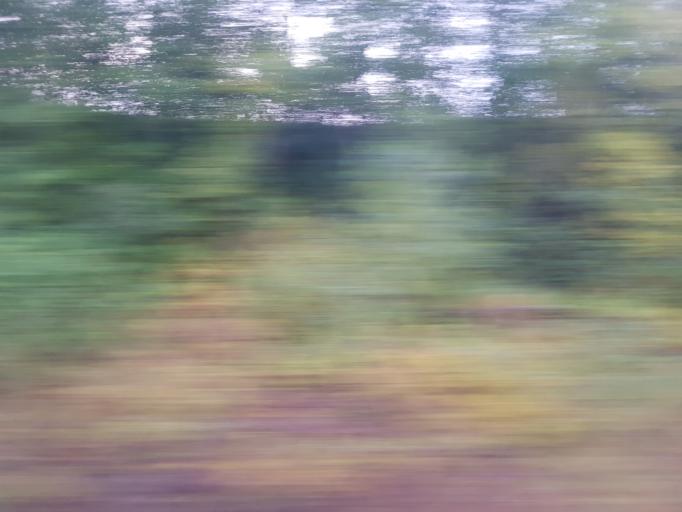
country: NO
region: Sor-Trondelag
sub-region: Melhus
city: Lundamo
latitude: 63.1457
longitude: 10.2745
